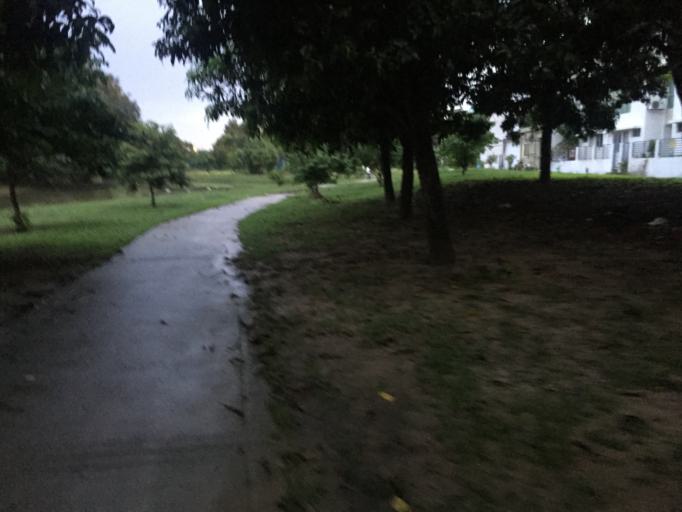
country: MY
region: Selangor
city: Klang
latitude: 2.9879
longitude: 101.4350
